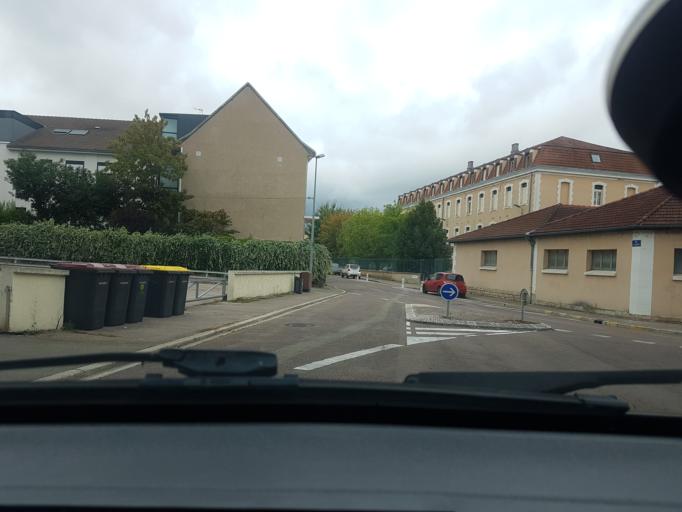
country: FR
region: Bourgogne
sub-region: Departement de l'Yonne
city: Auxerre
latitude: 47.7980
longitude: 3.5632
